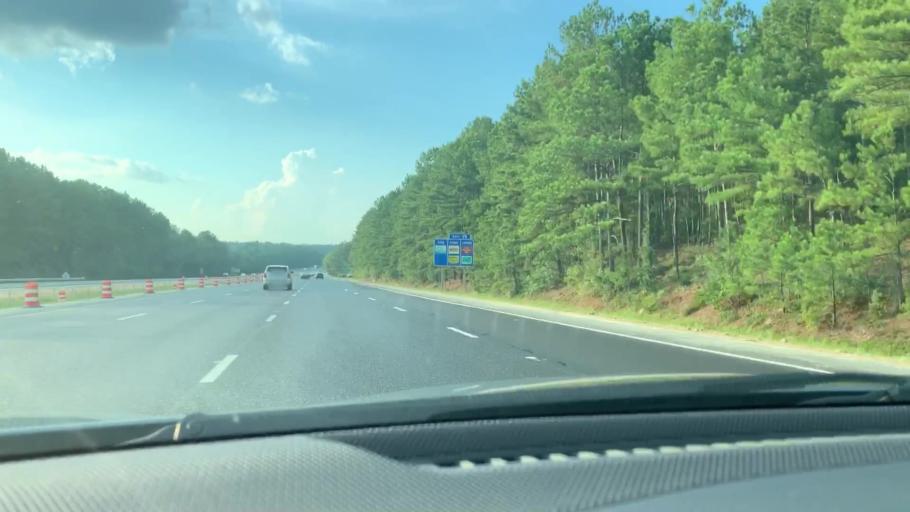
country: US
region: South Carolina
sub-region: Richland County
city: Dentsville
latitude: 34.0848
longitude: -80.9441
